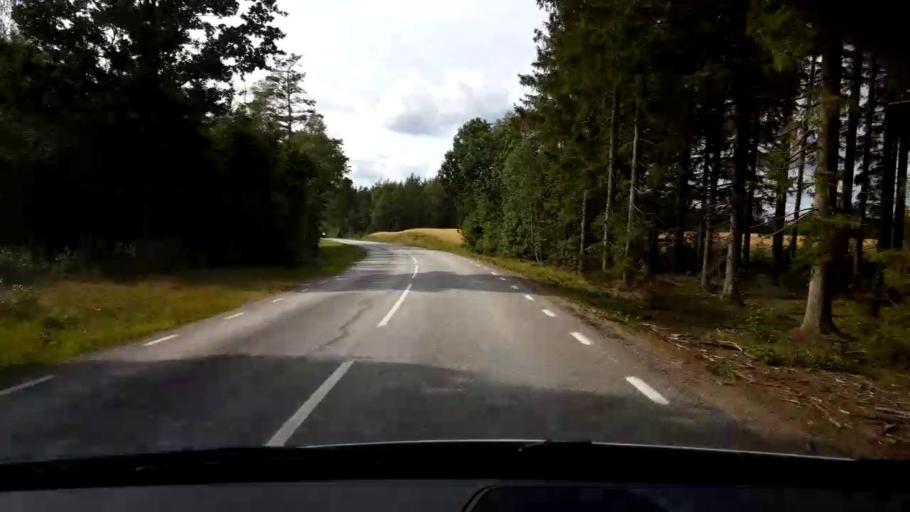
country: SE
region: Joenkoeping
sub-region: Vetlanda Kommun
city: Vetlanda
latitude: 57.3788
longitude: 15.0368
